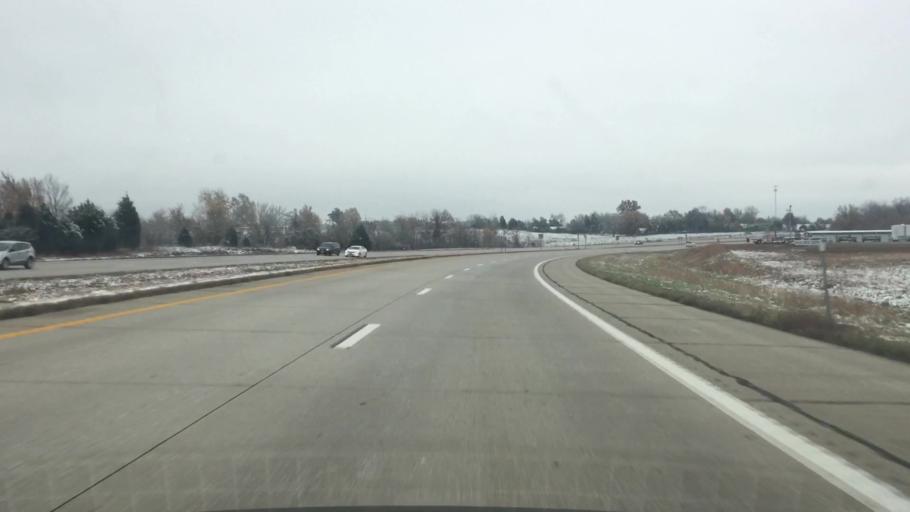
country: US
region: Missouri
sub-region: Saint Clair County
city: Osceola
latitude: 38.1775
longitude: -93.7239
